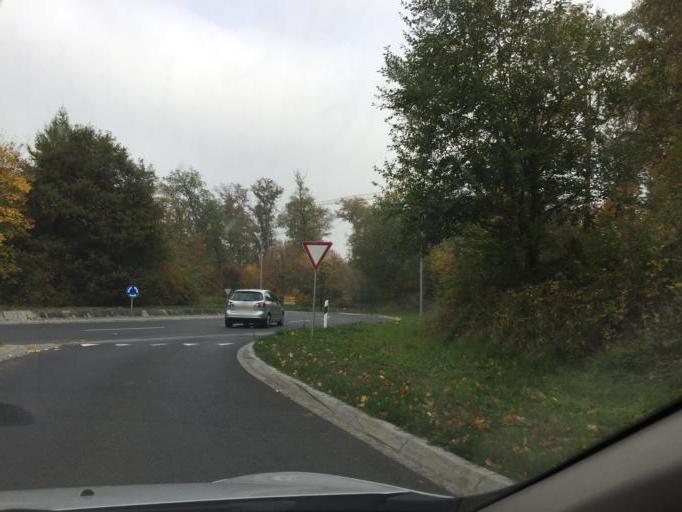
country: LU
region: Luxembourg
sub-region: Canton de Luxembourg
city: Sandweiler
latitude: 49.6085
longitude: 6.2304
